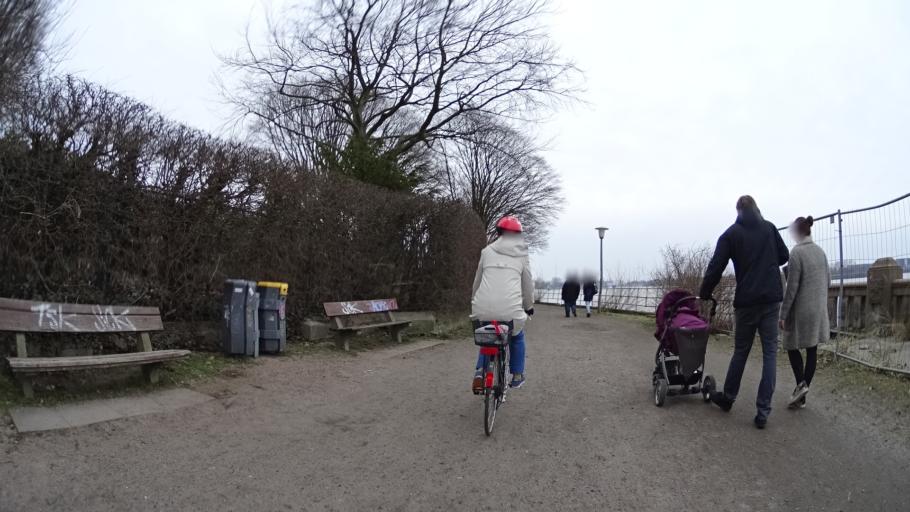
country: DE
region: Hamburg
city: Altona
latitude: 53.5472
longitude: 9.8680
